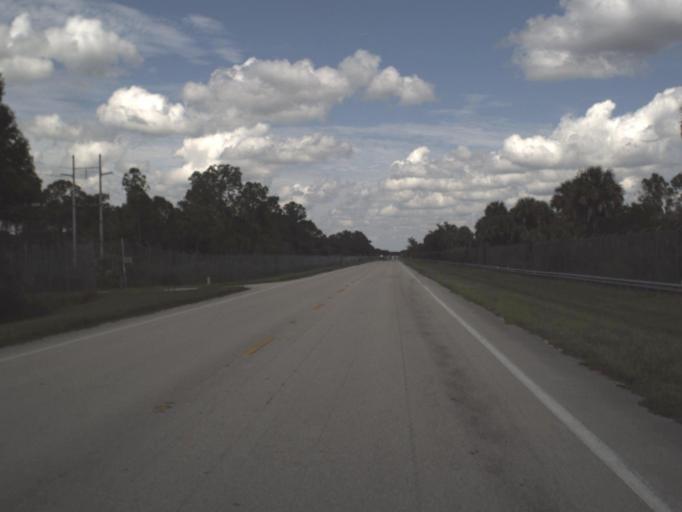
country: US
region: Florida
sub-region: Collier County
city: Immokalee
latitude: 26.1842
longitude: -81.3457
